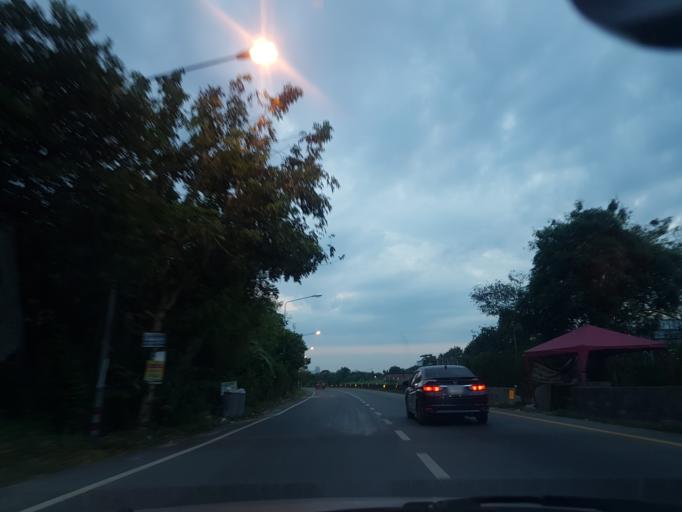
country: TH
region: Chon Buri
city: Phatthaya
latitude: 12.8942
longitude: 100.9001
